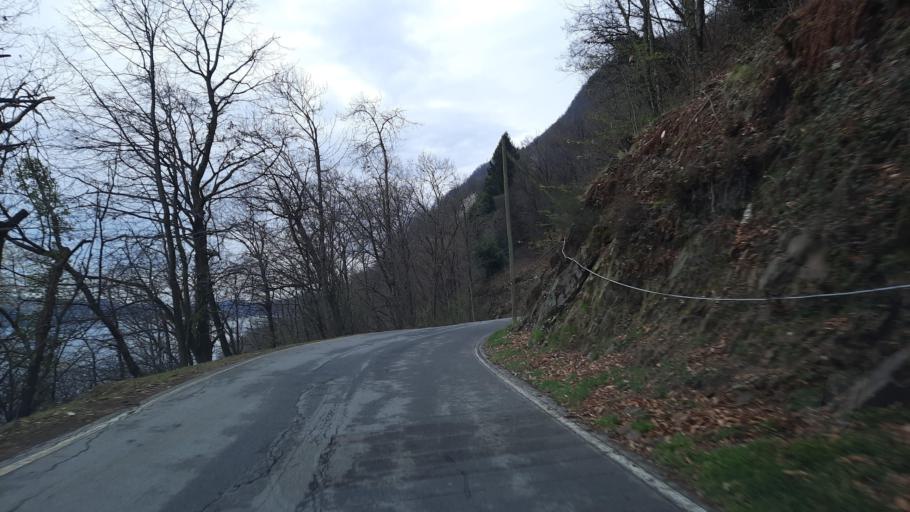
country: IT
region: Piedmont
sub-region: Provincia Verbano-Cusio-Ossola
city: Cesara
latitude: 45.8252
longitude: 8.3813
